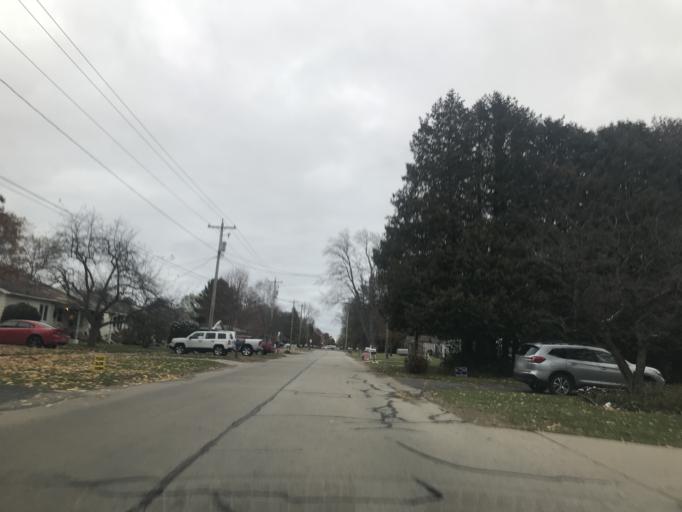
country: US
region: Wisconsin
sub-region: Marinette County
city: Marinette
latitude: 45.0931
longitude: -87.6532
